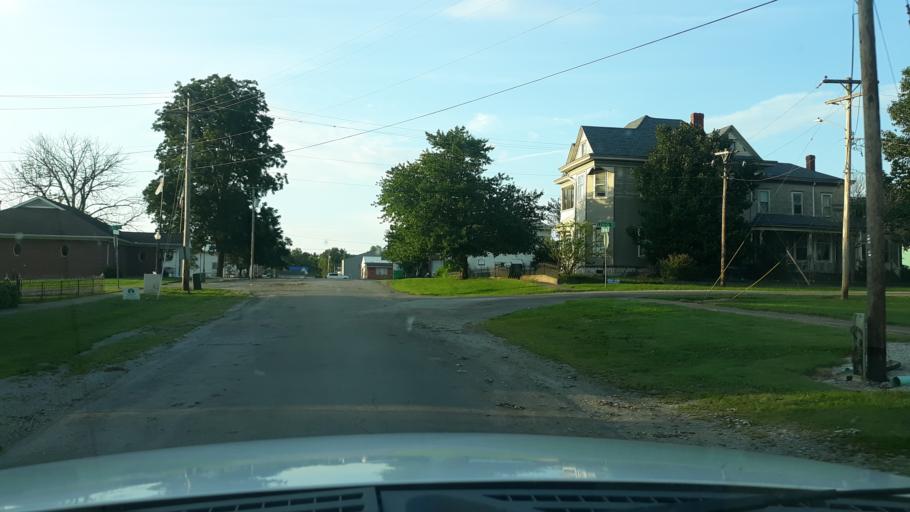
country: US
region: Illinois
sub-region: Saline County
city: Harrisburg
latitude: 37.8384
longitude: -88.6120
